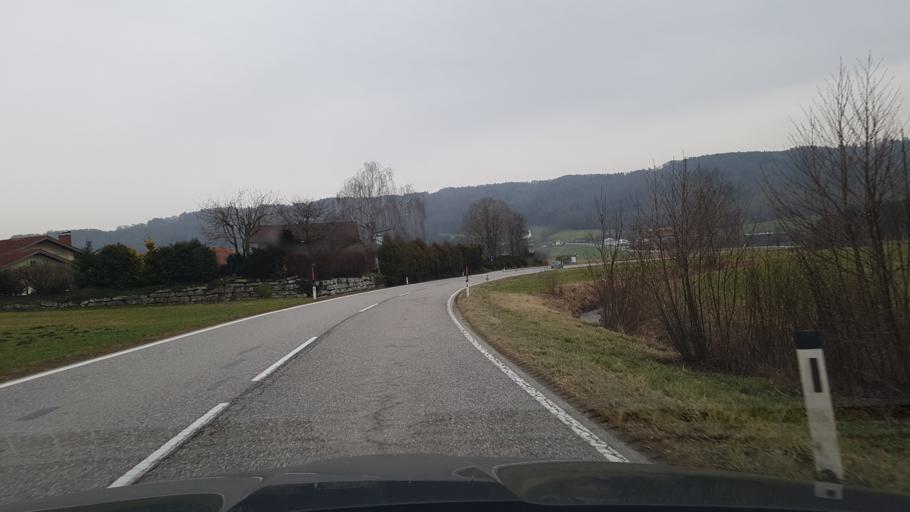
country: AT
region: Salzburg
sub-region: Politischer Bezirk Salzburg-Umgebung
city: Dorfbeuern
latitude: 48.0089
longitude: 13.0266
